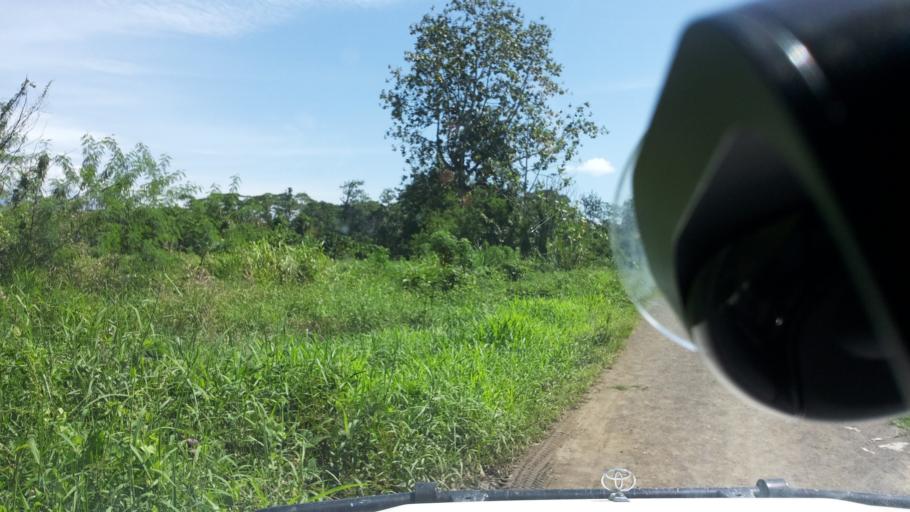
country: PG
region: Madang
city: Madang
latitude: -5.5250
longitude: 145.3729
